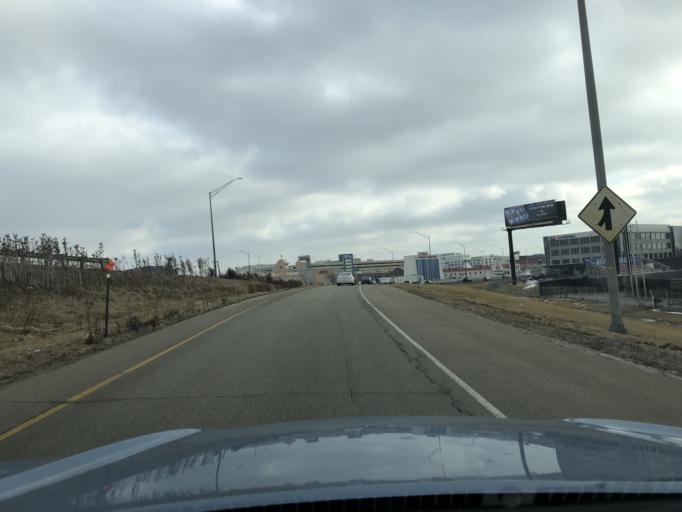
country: US
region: Illinois
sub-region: Cook County
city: Rosemont
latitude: 41.9819
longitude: -87.8721
